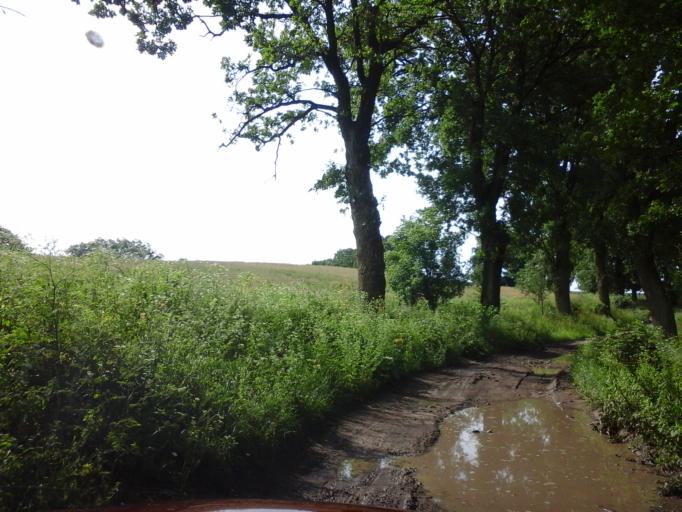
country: PL
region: West Pomeranian Voivodeship
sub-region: Powiat choszczenski
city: Krzecin
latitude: 53.1090
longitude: 15.5396
